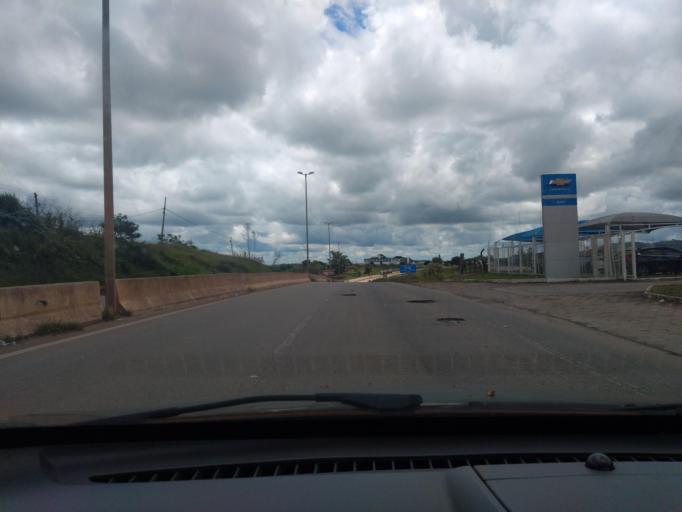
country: BR
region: Minas Gerais
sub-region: Lavras
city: Lavras
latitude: -21.2351
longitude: -45.0314
